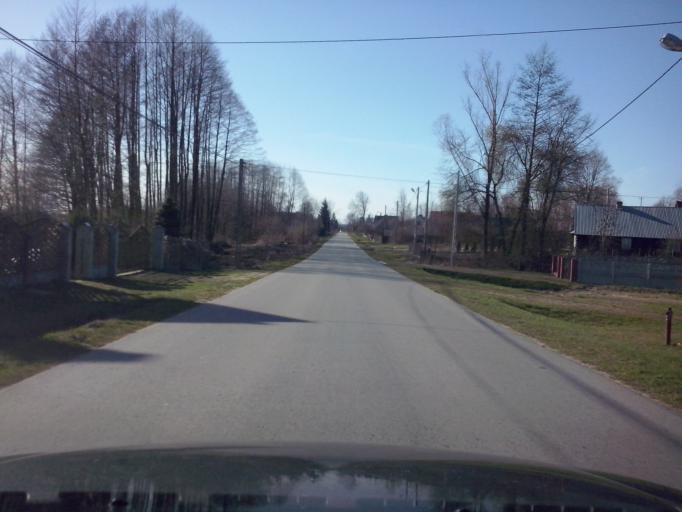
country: PL
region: Subcarpathian Voivodeship
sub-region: Powiat nizanski
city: Krzeszow
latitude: 50.3787
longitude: 22.3927
